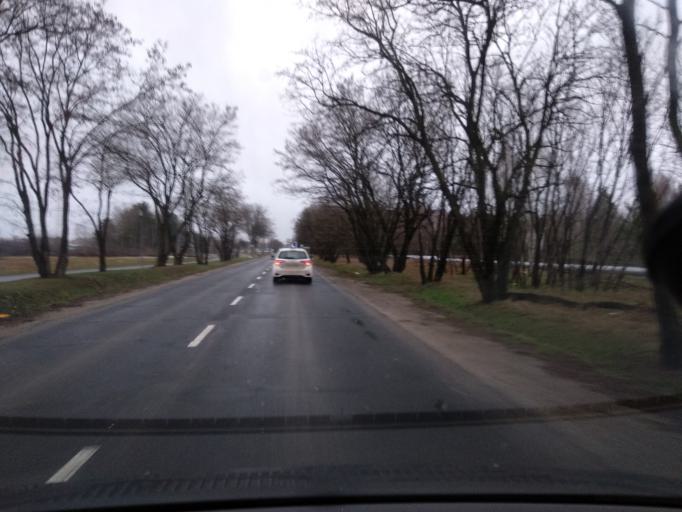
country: PL
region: Lower Silesian Voivodeship
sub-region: Powiat polkowicki
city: Polkowice
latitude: 51.5067
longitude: 16.0873
